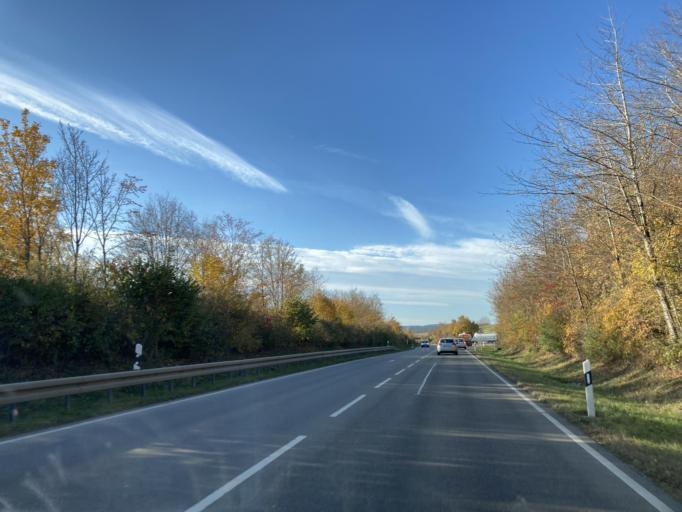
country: DE
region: Baden-Wuerttemberg
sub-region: Karlsruhe Region
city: Dornstetten
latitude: 48.4711
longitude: 8.5092
